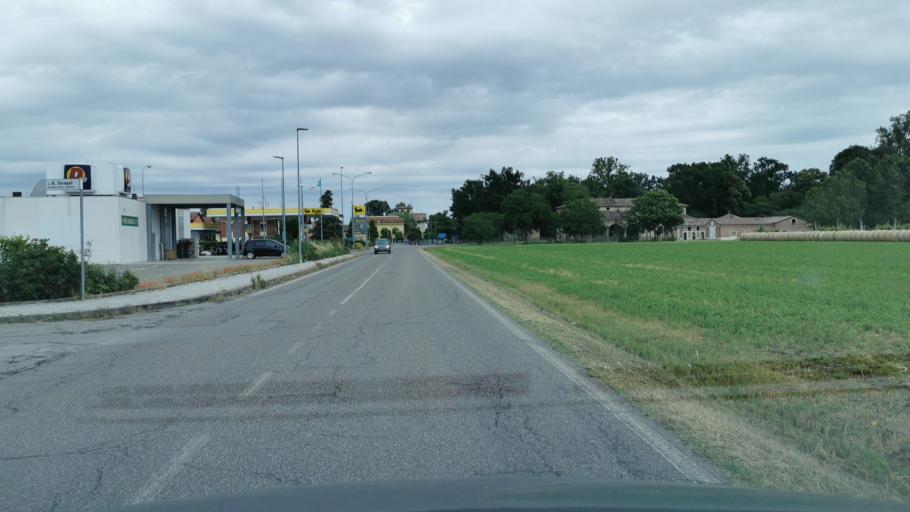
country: IT
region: Emilia-Romagna
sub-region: Provincia di Parma
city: Soragna
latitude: 44.9260
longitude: 10.1180
